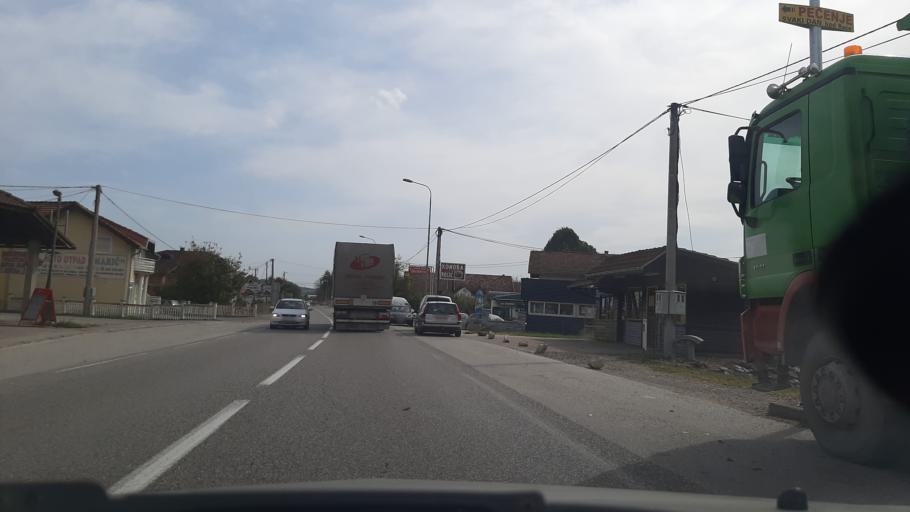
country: BA
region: Republika Srpska
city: Laktasi
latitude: 44.8796
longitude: 17.2870
